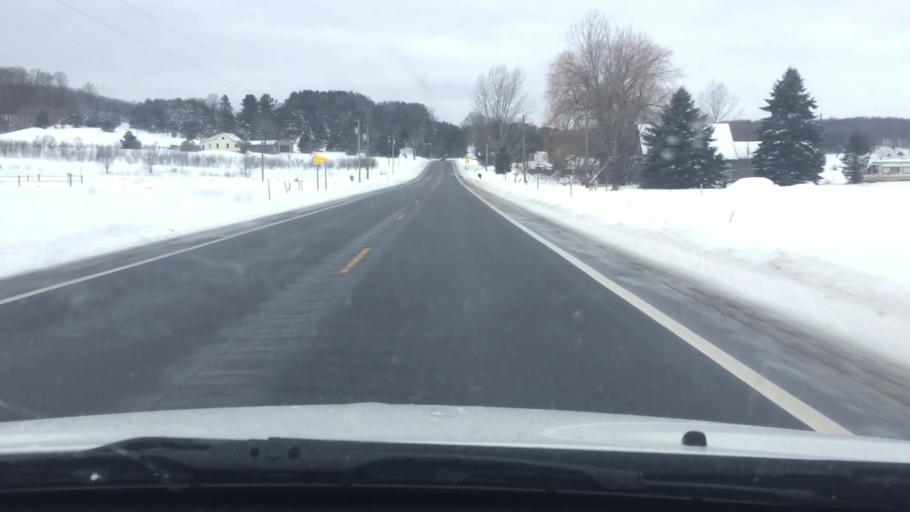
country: US
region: Michigan
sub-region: Charlevoix County
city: East Jordan
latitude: 45.1035
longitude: -85.0438
